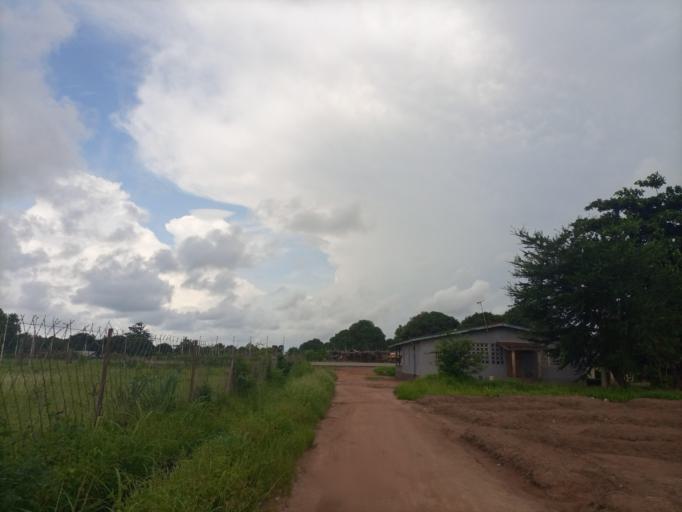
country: SL
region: Northern Province
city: Masoyila
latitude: 8.6105
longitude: -13.1770
